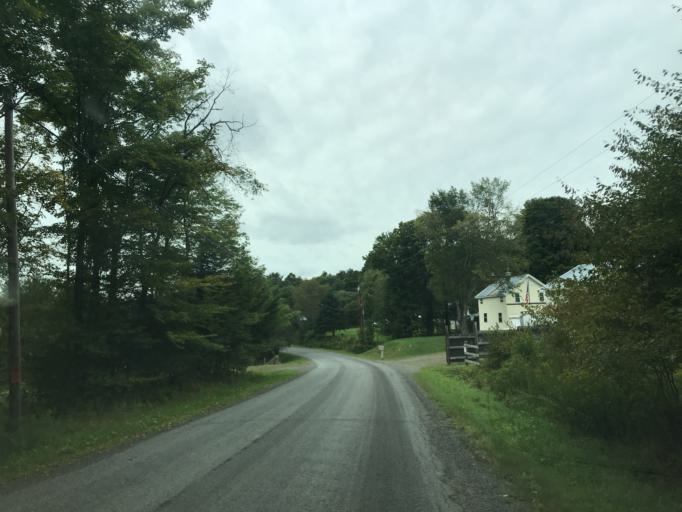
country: US
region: New York
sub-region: Otsego County
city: Worcester
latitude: 42.5173
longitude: -74.6654
